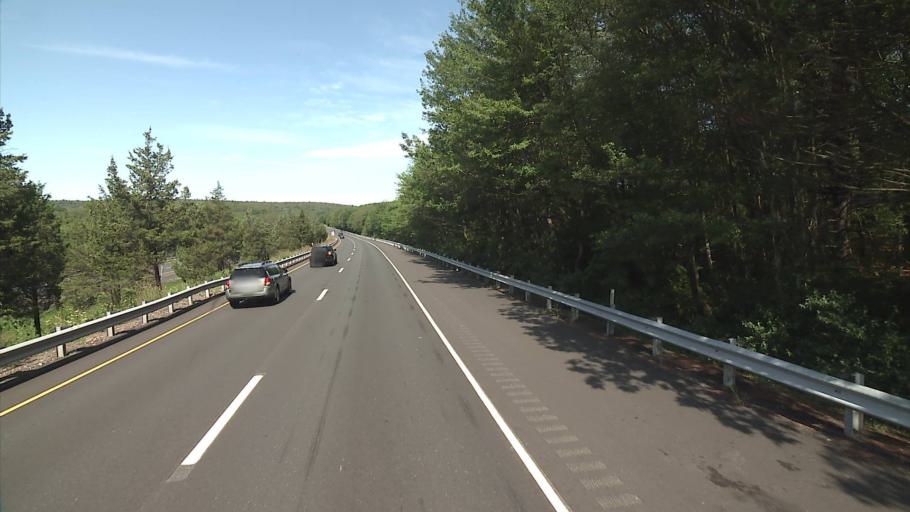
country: US
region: Connecticut
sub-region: Hartford County
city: Terramuggus
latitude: 41.6494
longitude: -72.4782
